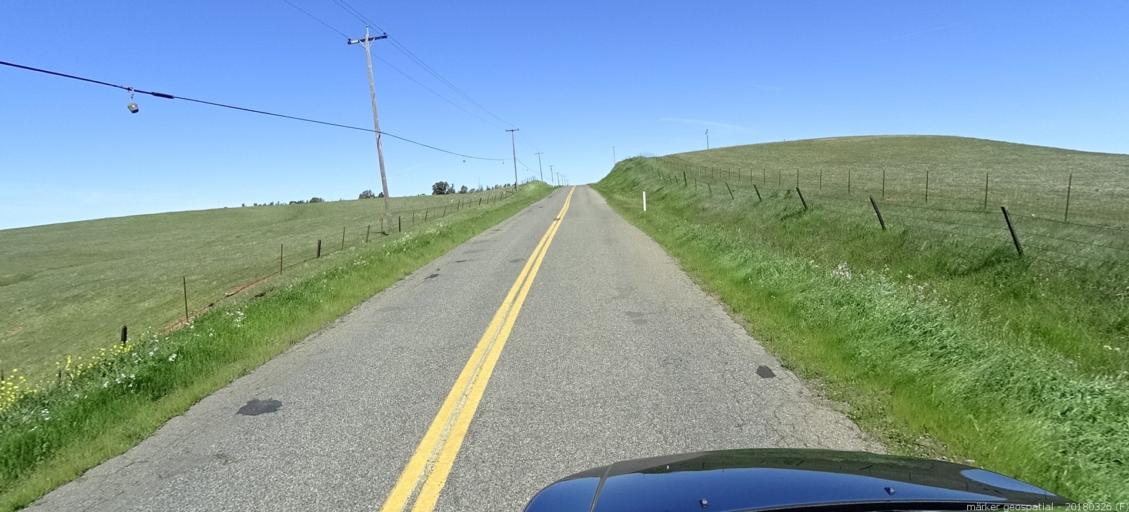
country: US
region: California
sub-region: Sacramento County
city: Wilton
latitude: 38.4904
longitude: -121.2135
